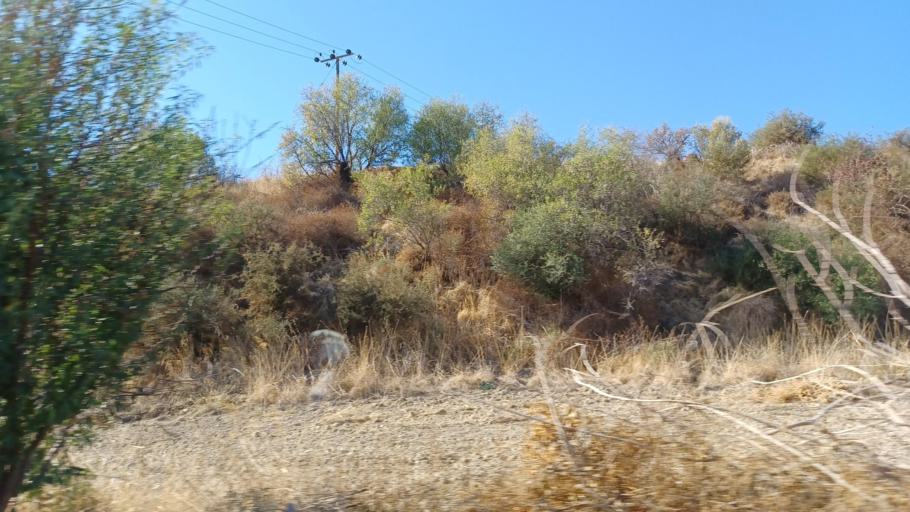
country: CY
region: Pafos
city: Polis
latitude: 35.0250
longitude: 32.4218
